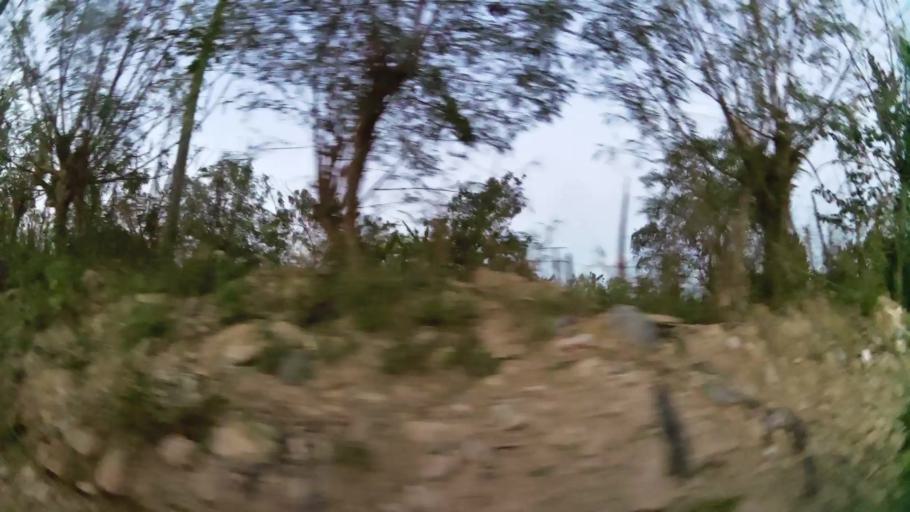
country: DO
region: Nacional
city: La Agustina
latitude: 18.5451
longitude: -69.9394
